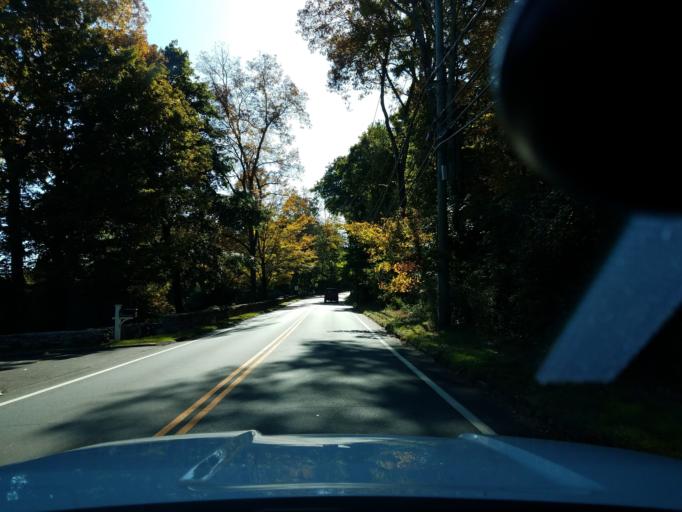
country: US
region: Connecticut
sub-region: Fairfield County
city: Cos Cob
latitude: 41.0844
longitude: -73.6260
